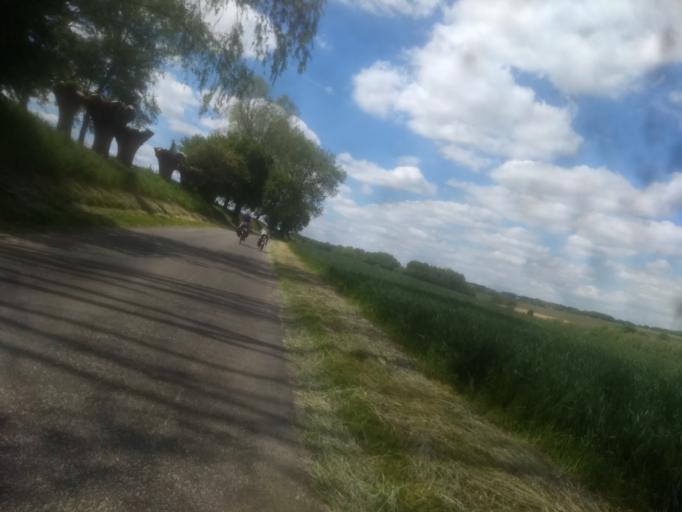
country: FR
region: Nord-Pas-de-Calais
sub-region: Departement du Pas-de-Calais
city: Beaumetz-les-Loges
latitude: 50.2274
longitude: 2.6704
